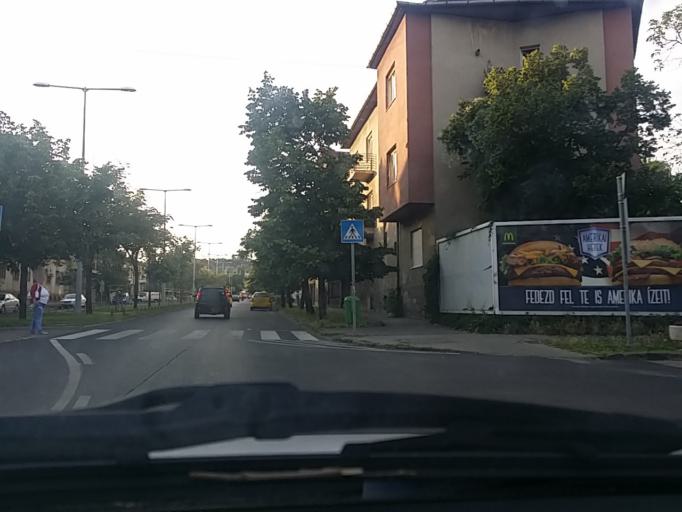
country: HU
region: Budapest
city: Budapest XI. keruelet
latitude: 47.4794
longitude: 19.0314
